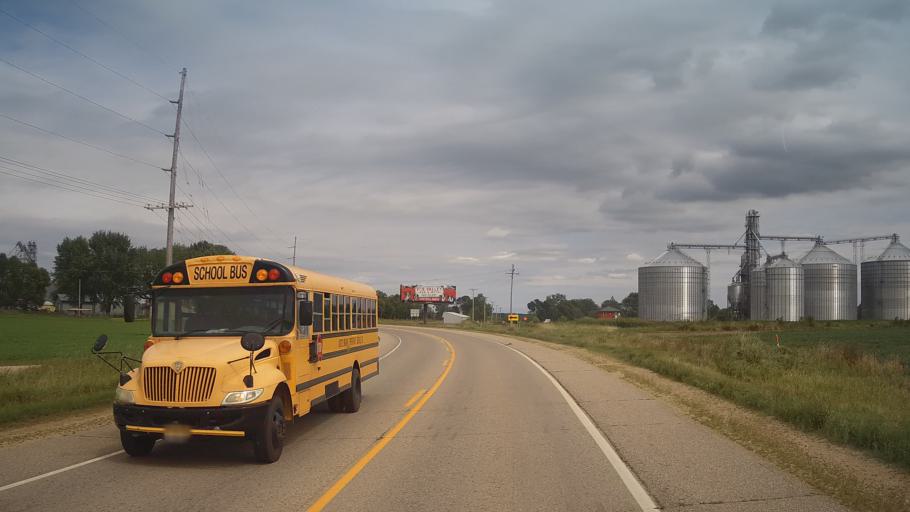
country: US
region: Wisconsin
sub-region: Green Lake County
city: Berlin
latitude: 44.0411
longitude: -88.9889
